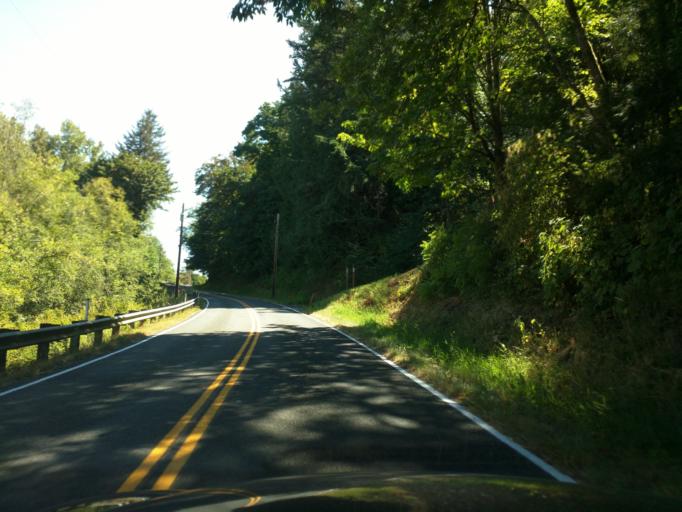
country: US
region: Washington
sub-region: Whatcom County
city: Geneva
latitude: 48.8039
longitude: -122.4086
